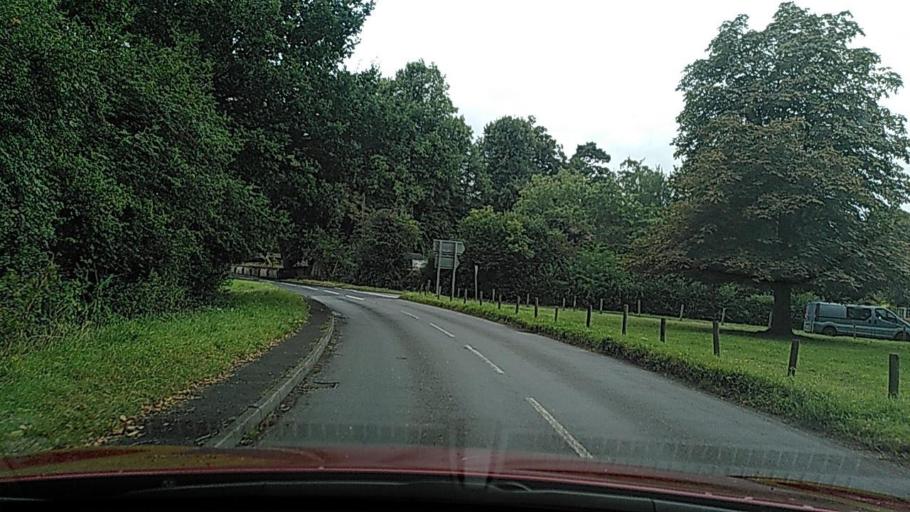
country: GB
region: England
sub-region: Oxfordshire
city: Rotherfield Peppard
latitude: 51.5542
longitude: -0.9915
